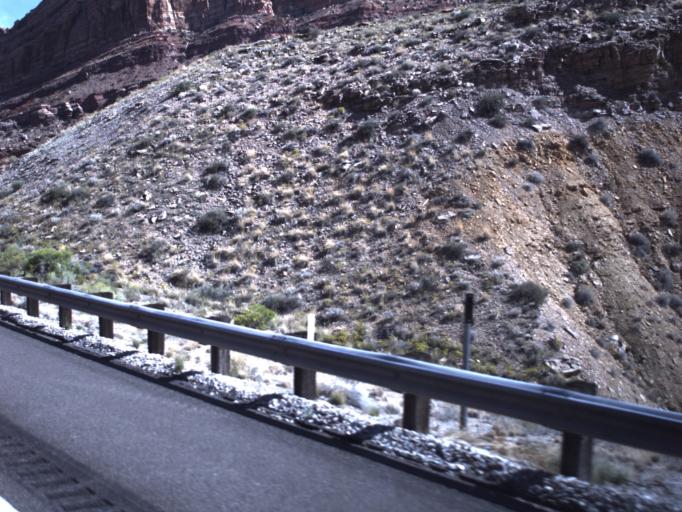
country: US
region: Utah
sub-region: Carbon County
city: East Carbon City
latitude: 38.9279
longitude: -110.4564
